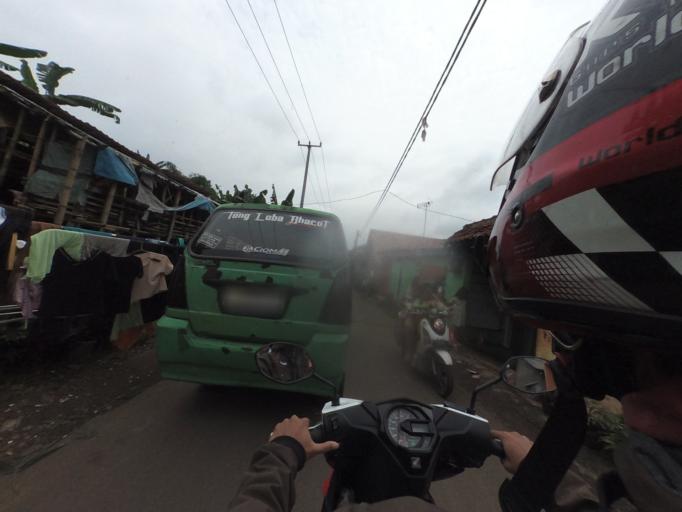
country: ID
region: West Java
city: Bogor
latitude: -6.6142
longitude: 106.7506
